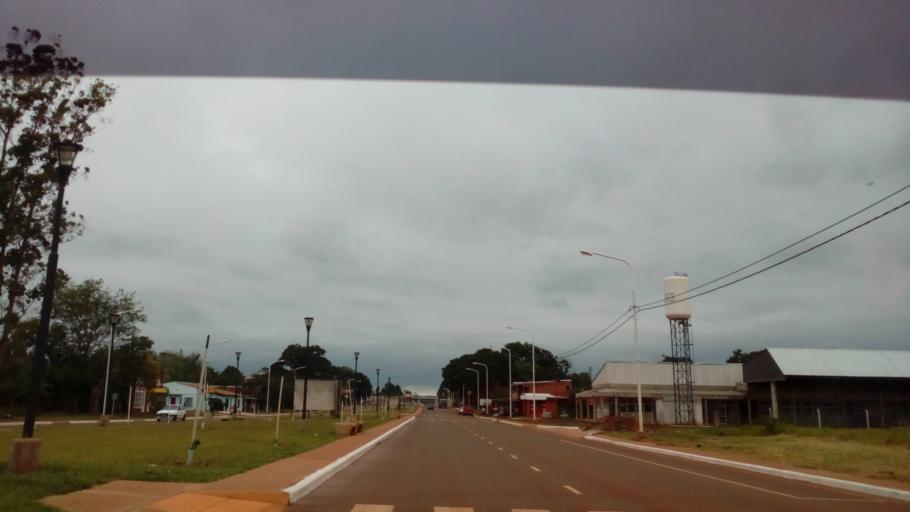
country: AR
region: Misiones
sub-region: Departamento de Candelaria
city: Candelaria
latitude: -27.4663
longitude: -55.7455
